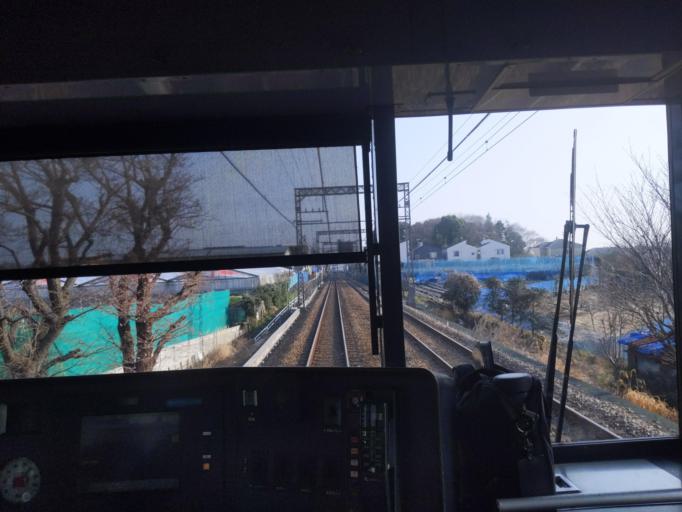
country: JP
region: Kanagawa
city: Minami-rinkan
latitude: 35.4191
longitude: 139.4657
